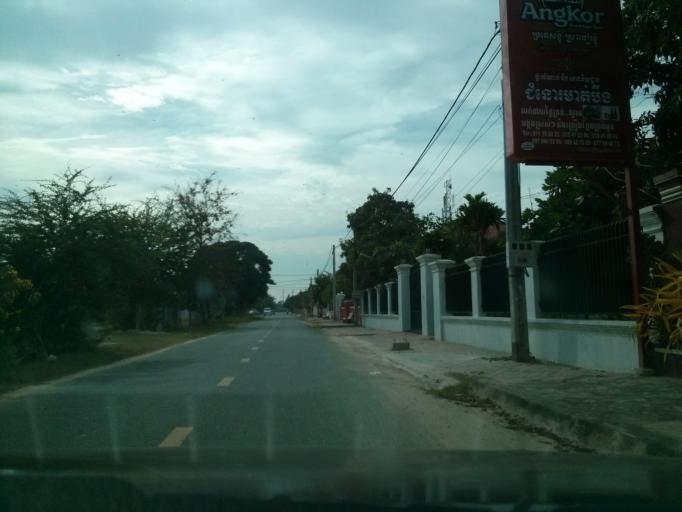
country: KH
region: Takeo
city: Takeo
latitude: 10.9899
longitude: 104.7877
